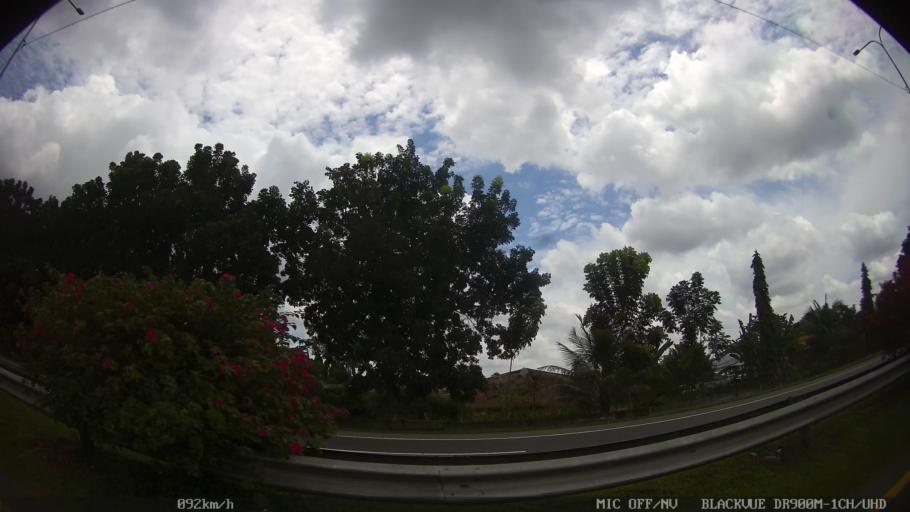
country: ID
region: North Sumatra
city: Medan
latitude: 3.6218
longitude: 98.7200
